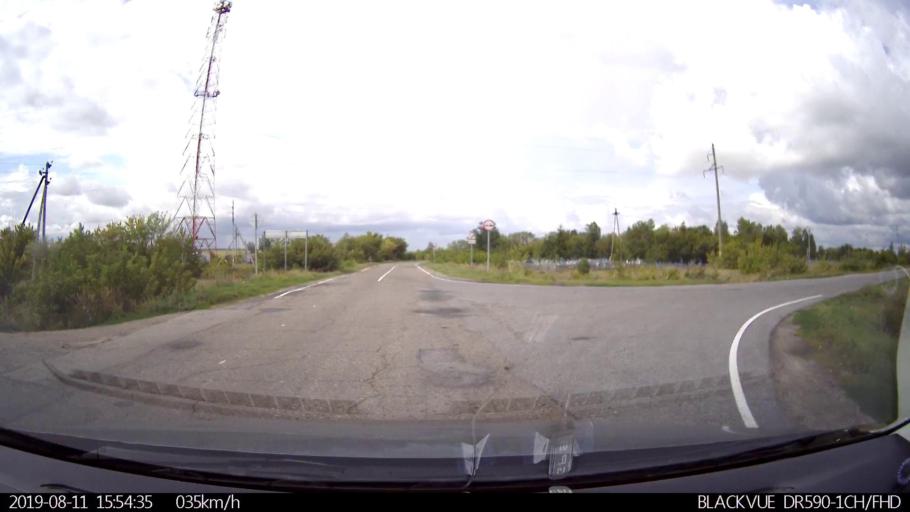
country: RU
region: Ulyanovsk
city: Ignatovka
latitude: 53.9419
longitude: 47.6562
